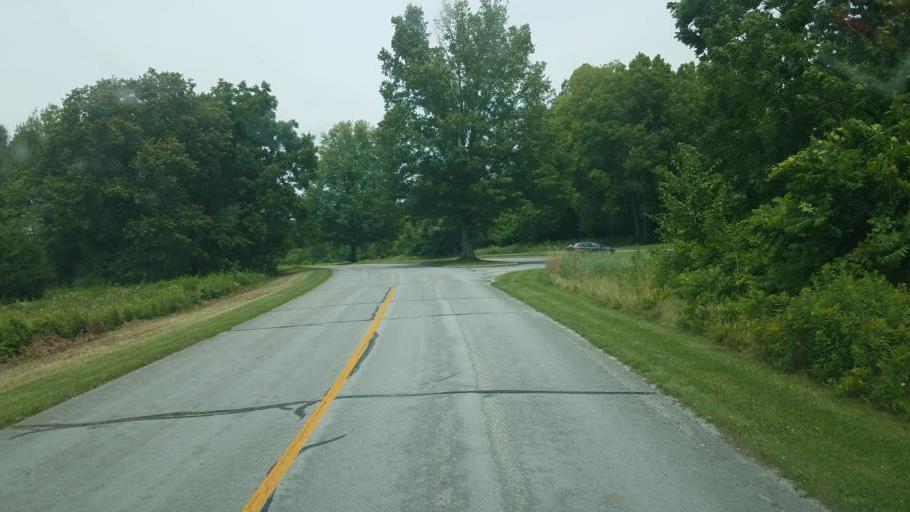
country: US
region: Ohio
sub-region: Delaware County
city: Powell
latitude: 40.1536
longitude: -83.0391
